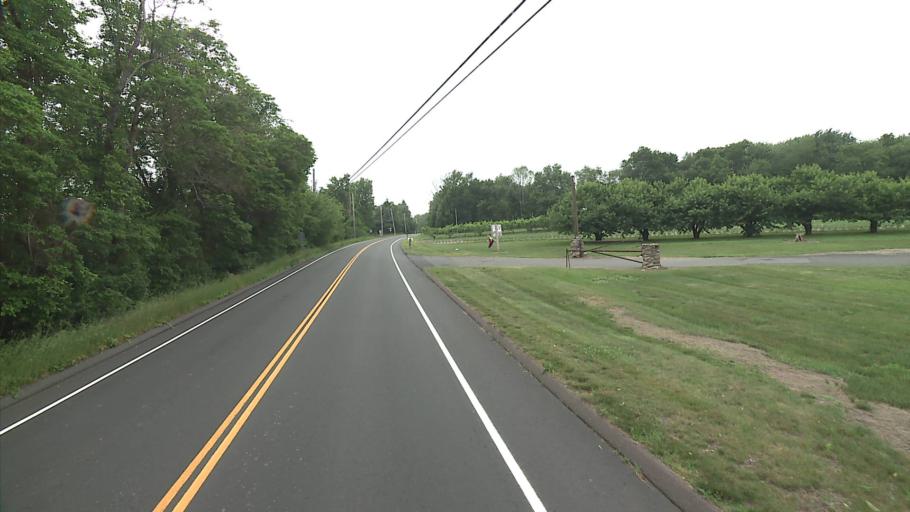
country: US
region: Connecticut
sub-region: Hartford County
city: Terramuggus
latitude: 41.7035
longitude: -72.4704
